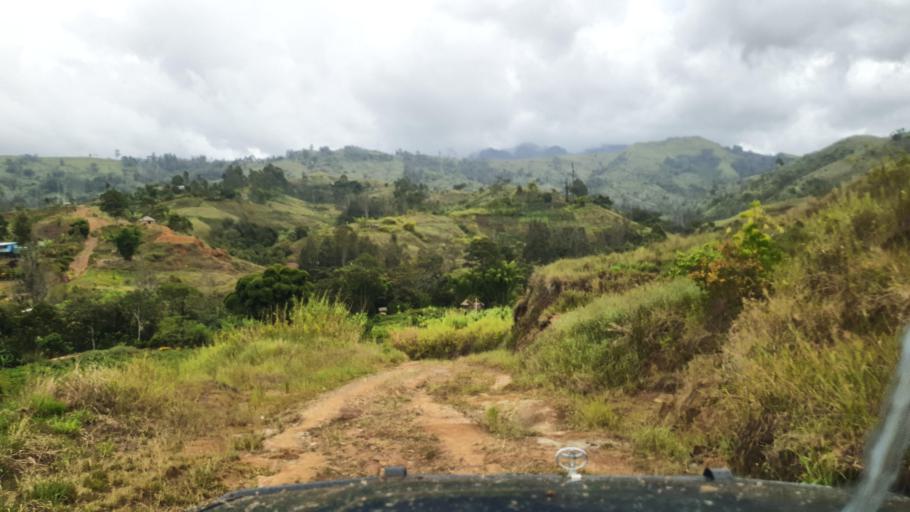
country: PG
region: Jiwaka
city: Minj
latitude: -5.9514
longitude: 144.7748
